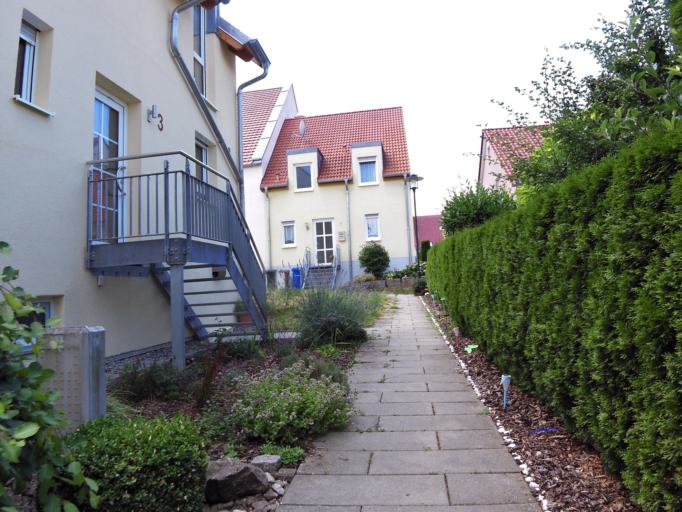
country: DE
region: Bavaria
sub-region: Regierungsbezirk Unterfranken
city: Gerbrunn
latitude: 49.7844
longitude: 9.9902
